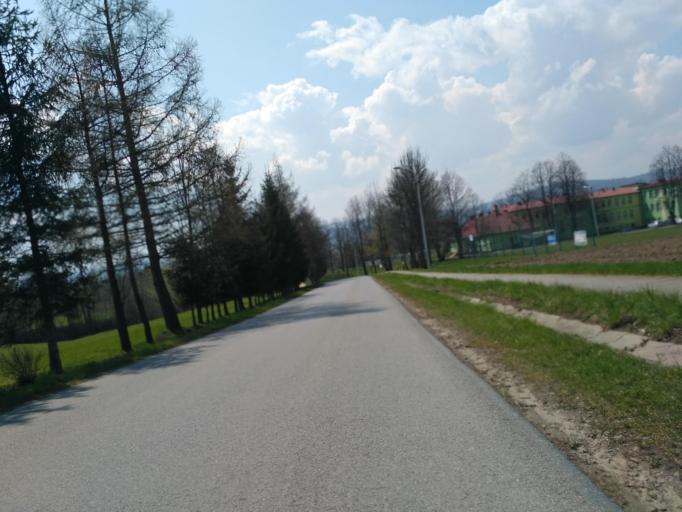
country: PL
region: Subcarpathian Voivodeship
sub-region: Powiat sanocki
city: Zarszyn
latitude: 49.5460
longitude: 21.9793
